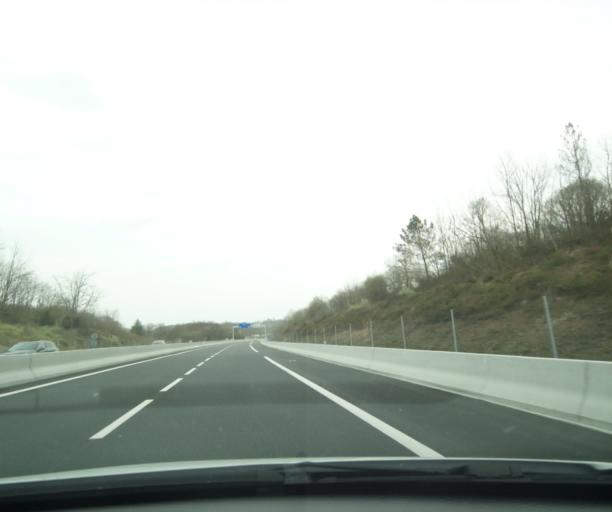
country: FR
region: Aquitaine
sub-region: Departement des Pyrenees-Atlantiques
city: Lahonce
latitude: 43.4527
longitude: -1.3881
